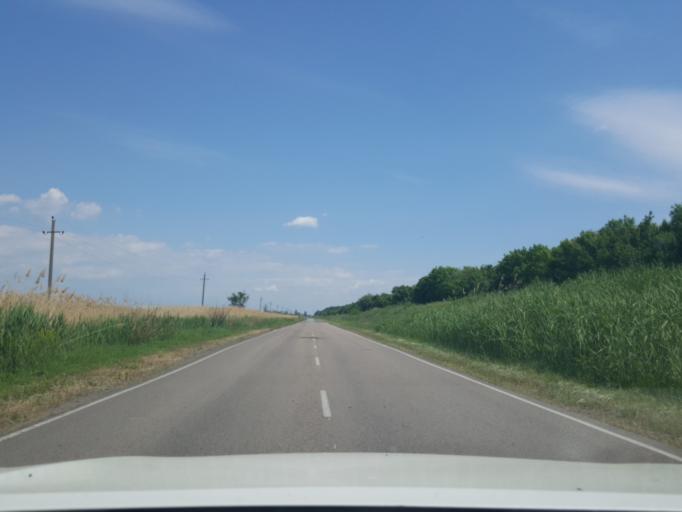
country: RO
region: Tulcea
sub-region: Comuna Luncavita
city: Rachelu
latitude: 45.3102
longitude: 28.3954
